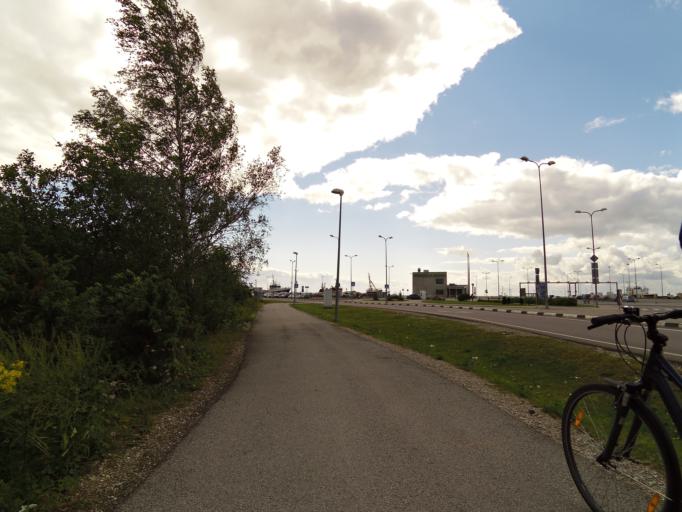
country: EE
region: Laeaene
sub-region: Haapsalu linn
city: Haapsalu
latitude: 58.9070
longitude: 23.4266
